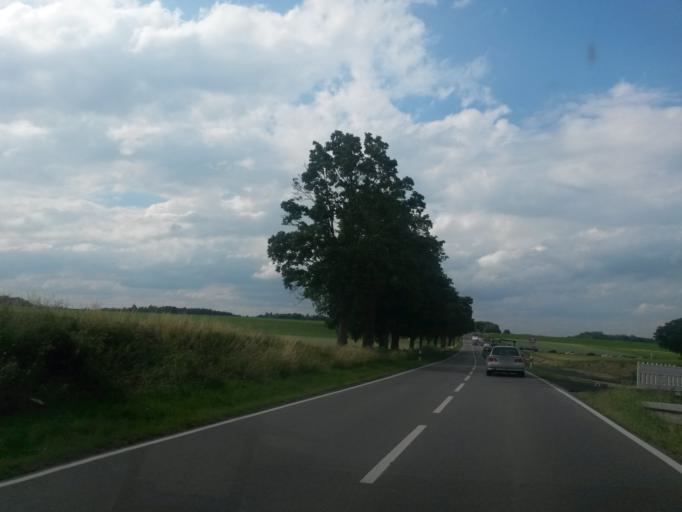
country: DE
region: Bavaria
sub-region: Upper Bavaria
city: Haimhausen
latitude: 48.3194
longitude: 11.5732
